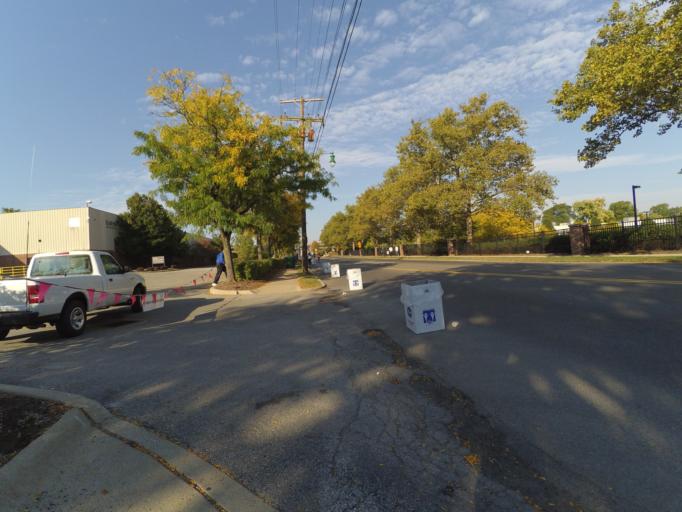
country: US
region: Ohio
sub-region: Franklin County
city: Grandview Heights
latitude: 39.9876
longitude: -83.0220
